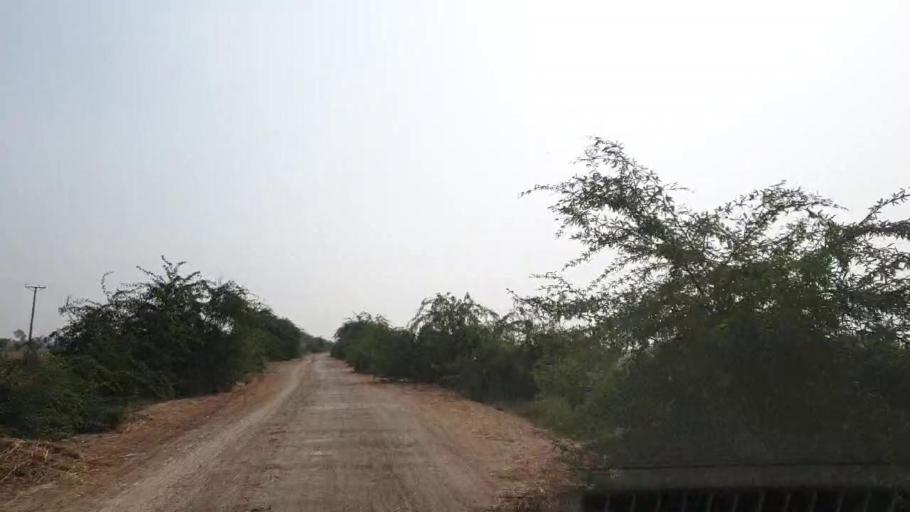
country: PK
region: Sindh
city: Matli
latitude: 24.9886
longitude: 68.5795
